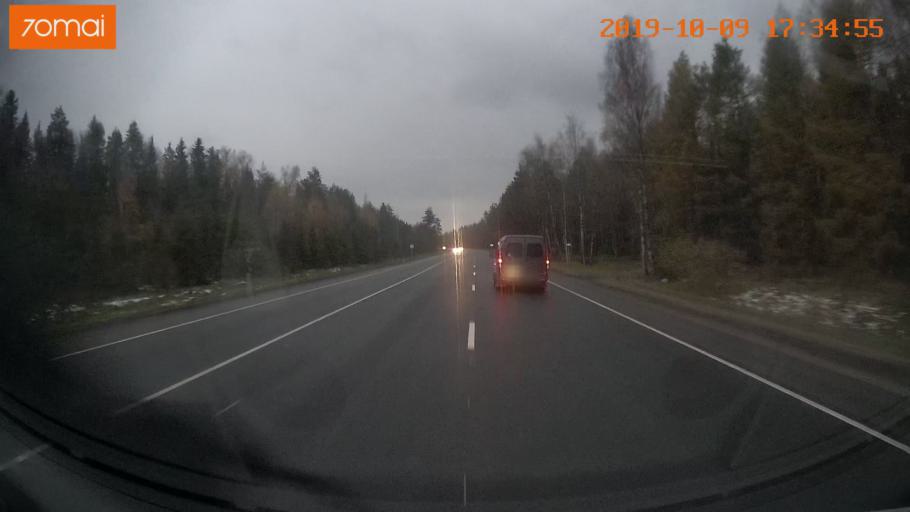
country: RU
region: Ivanovo
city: Bogorodskoye
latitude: 57.1014
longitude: 41.0071
